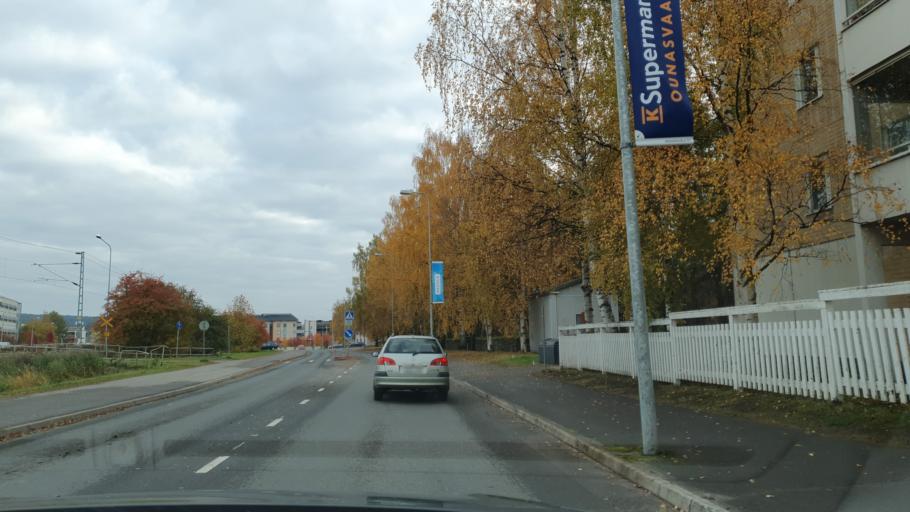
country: FI
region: Lapland
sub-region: Rovaniemi
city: Rovaniemi
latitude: 66.4955
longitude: 25.7241
